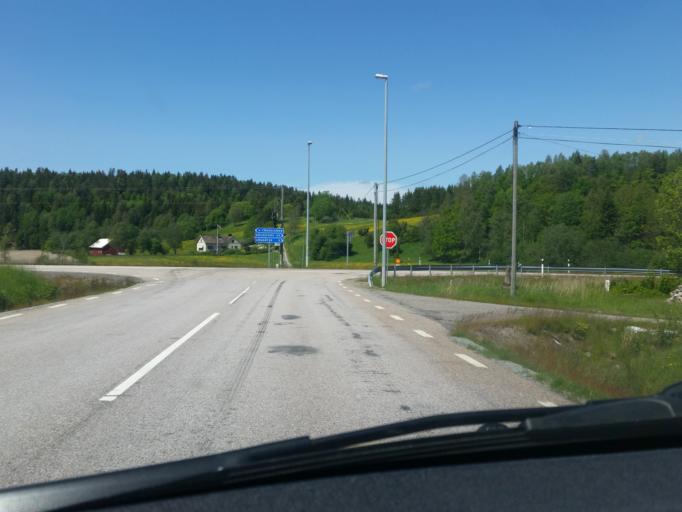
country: SE
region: Vaestra Goetaland
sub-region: Fargelanda Kommun
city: Faergelanda
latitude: 58.5942
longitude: 12.0409
